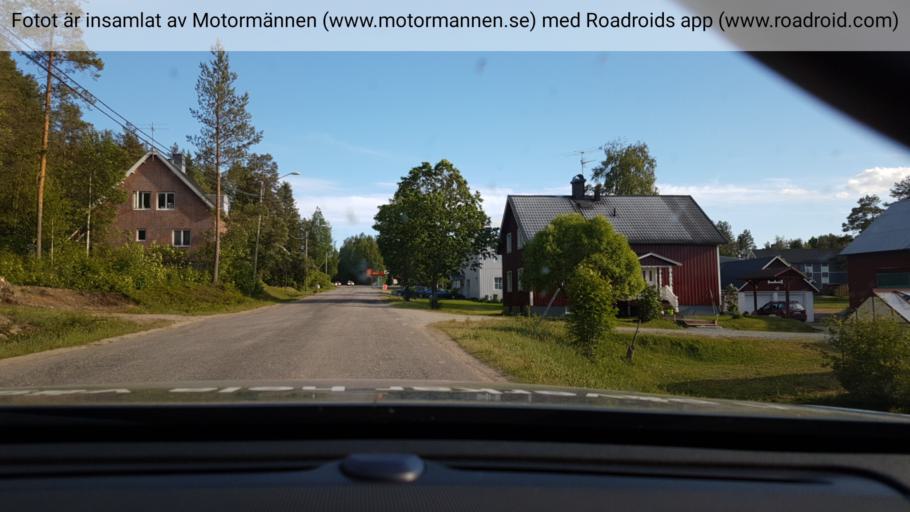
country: SE
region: Vaesterbotten
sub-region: Vannas Kommun
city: Vannasby
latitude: 64.0905
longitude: 19.9541
